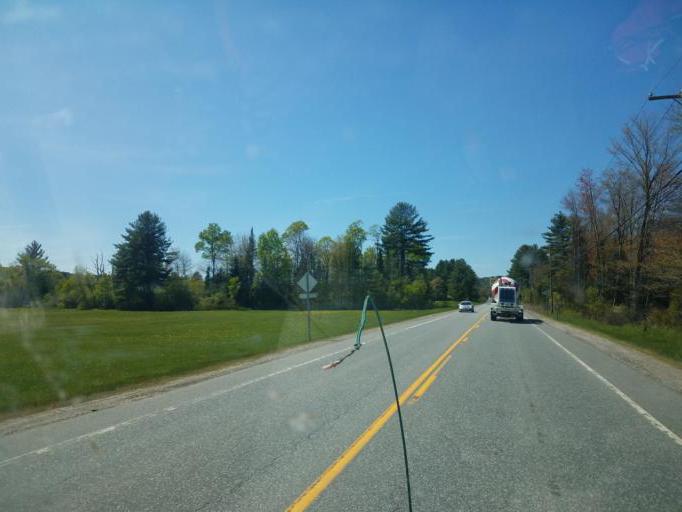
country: US
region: New Hampshire
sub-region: Grafton County
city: Enfield
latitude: 43.6478
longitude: -72.0534
